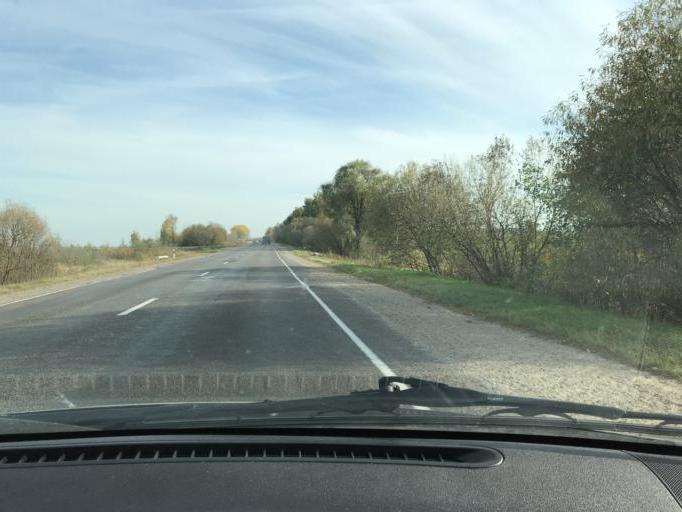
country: BY
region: Brest
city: Lahishyn
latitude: 52.2451
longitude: 25.9913
